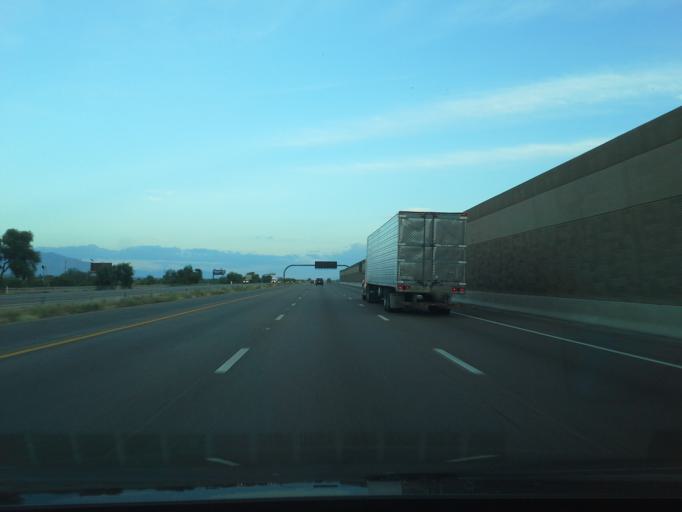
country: US
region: Arizona
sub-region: Pima County
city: Marana
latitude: 32.4558
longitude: -111.2077
